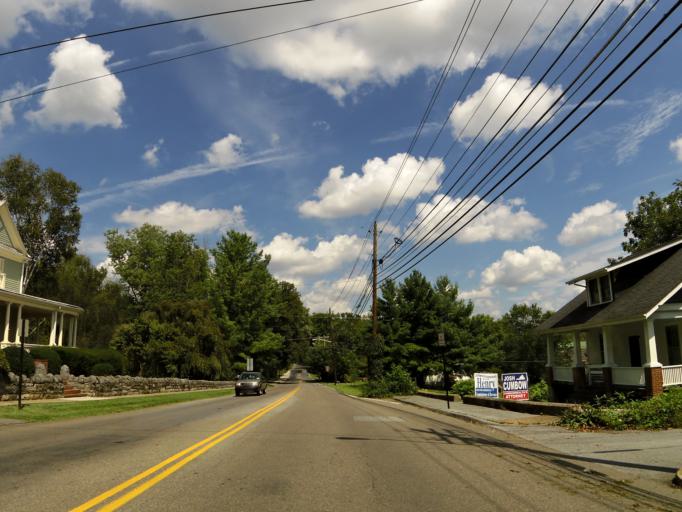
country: US
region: Virginia
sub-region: Washington County
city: Abingdon
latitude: 36.7145
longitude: -81.9669
